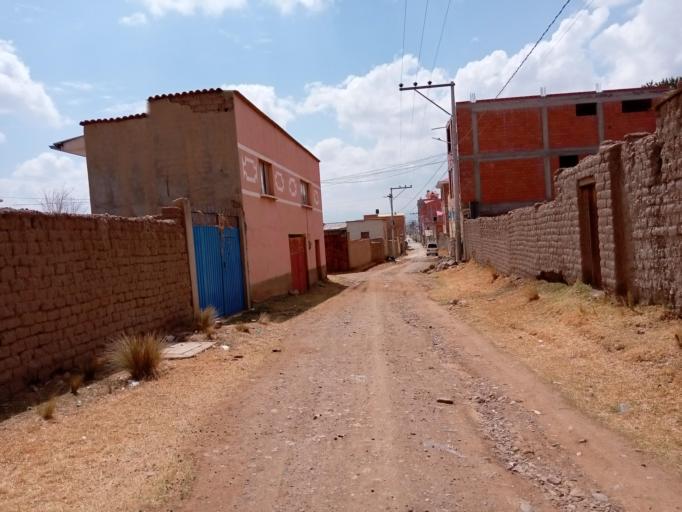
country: BO
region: La Paz
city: Batallas
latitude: -16.3998
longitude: -68.4794
